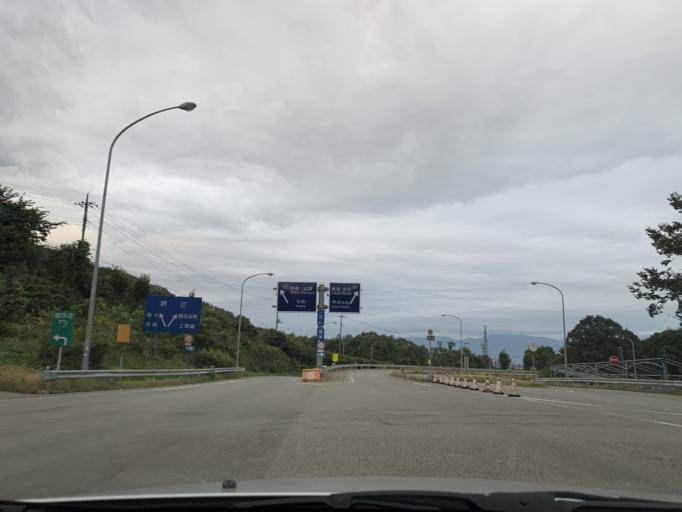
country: JP
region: Yamanashi
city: Enzan
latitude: 35.6522
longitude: 138.7344
